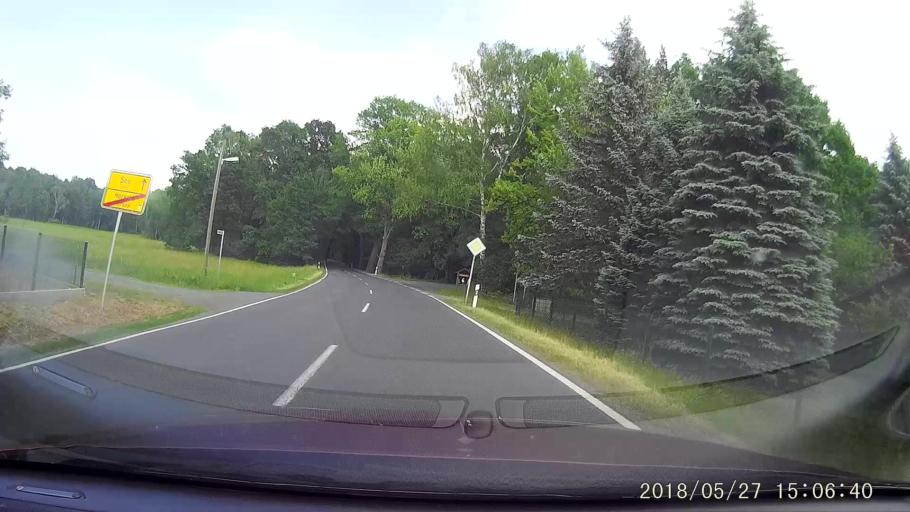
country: DE
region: Saxony
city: Mucka
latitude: 51.3027
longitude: 14.7336
